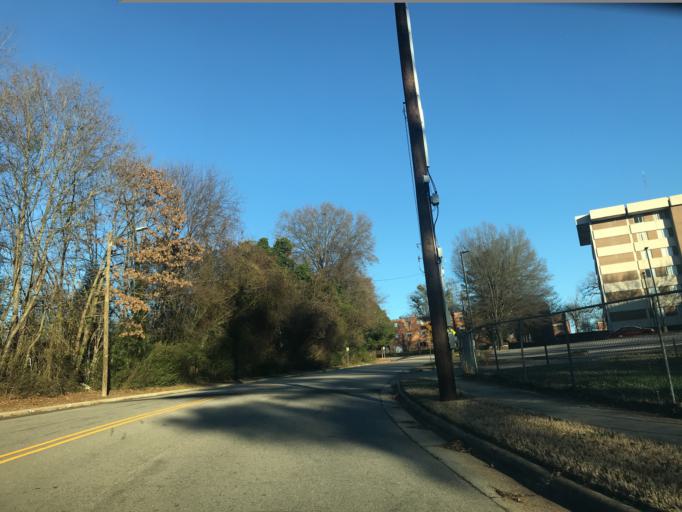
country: US
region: North Carolina
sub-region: Wake County
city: Raleigh
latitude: 35.7868
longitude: -78.6226
